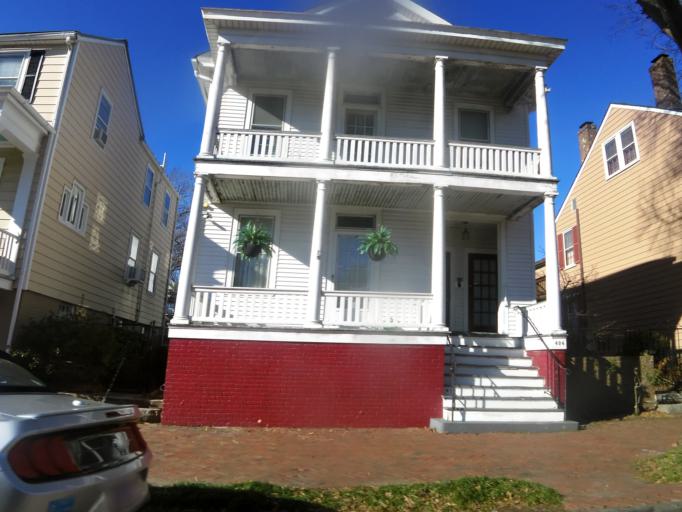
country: US
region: Virginia
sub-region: City of Portsmouth
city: Portsmouth
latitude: 36.8374
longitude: -76.3041
